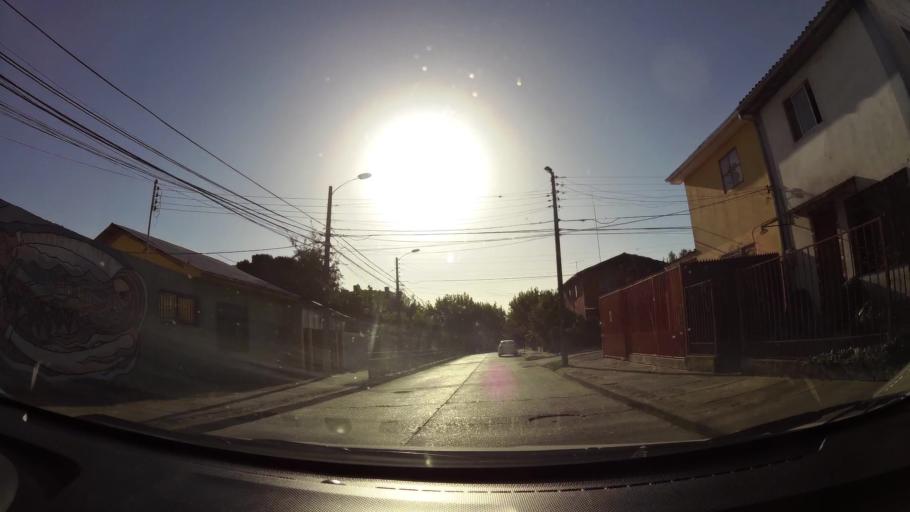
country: CL
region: Maule
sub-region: Provincia de Talca
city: Talca
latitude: -35.4365
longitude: -71.6584
